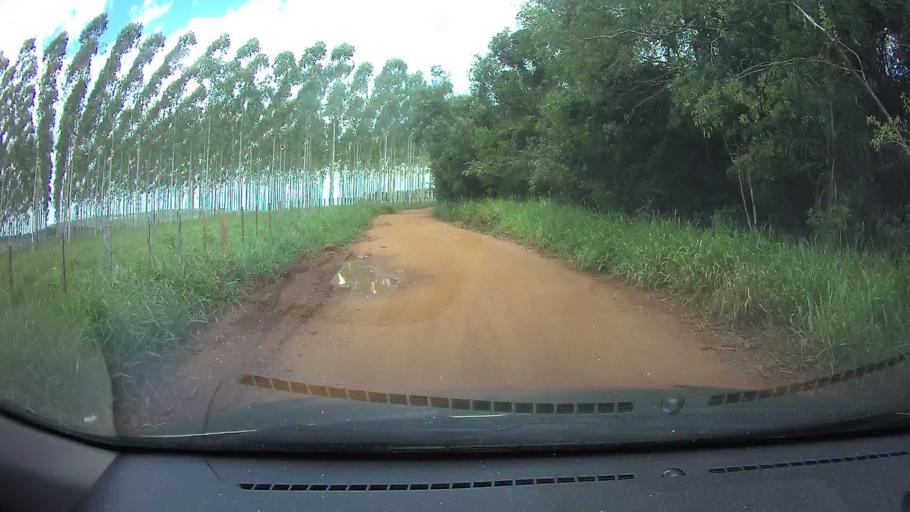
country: PY
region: Paraguari
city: La Colmena
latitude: -25.9654
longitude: -56.7351
